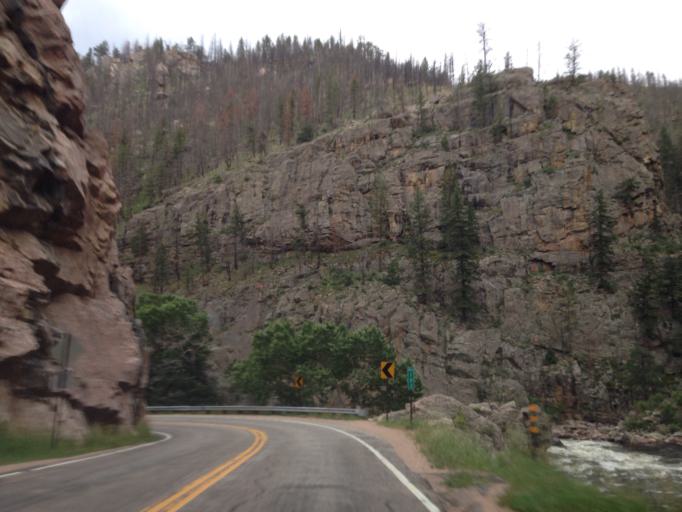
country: US
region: Colorado
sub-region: Larimer County
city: Laporte
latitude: 40.6752
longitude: -105.4295
